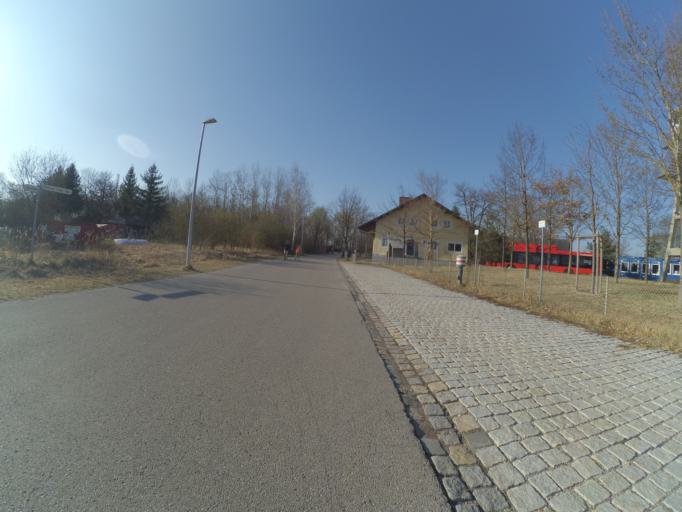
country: DE
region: Bavaria
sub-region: Upper Bavaria
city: Oberschleissheim
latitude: 48.2392
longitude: 11.5503
